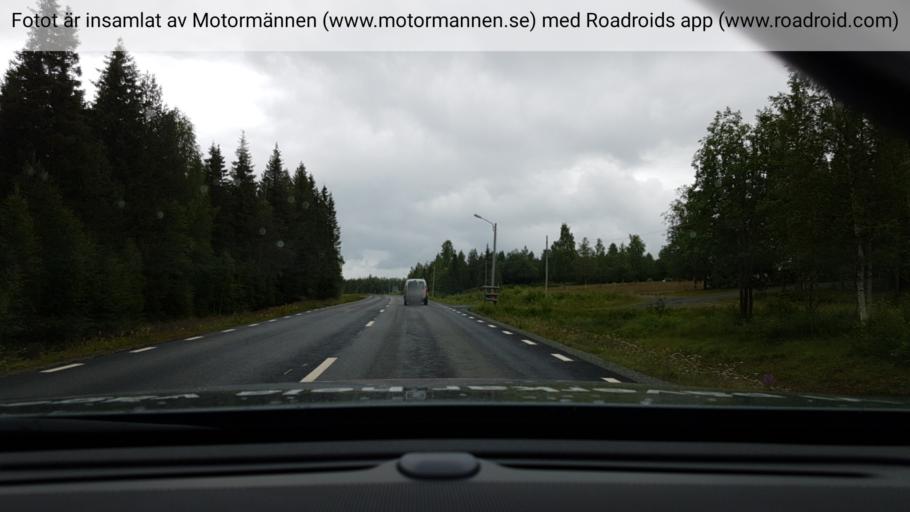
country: SE
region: Vaesterbotten
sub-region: Norsjo Kommun
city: Norsjoe
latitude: 65.3001
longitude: 19.5496
